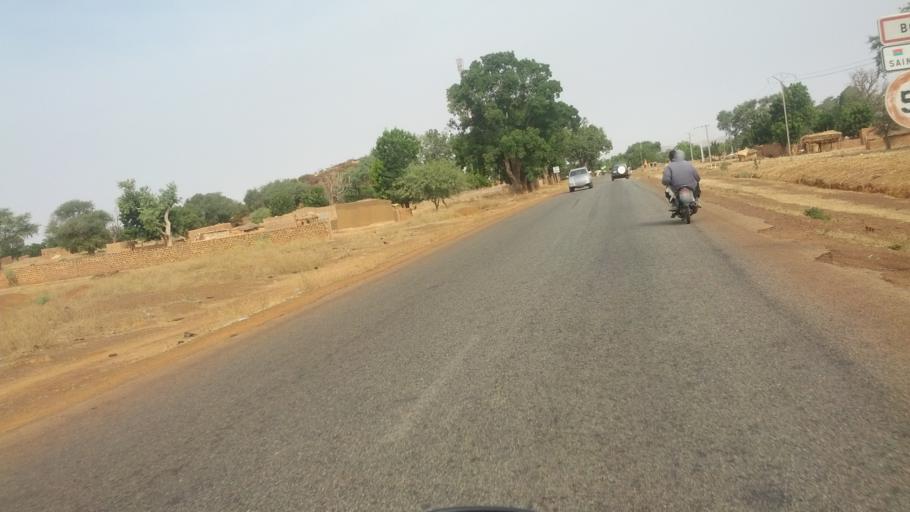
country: BF
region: Centre-Nord
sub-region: Province du Sanmatenga
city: Kaya
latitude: 12.8994
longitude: -1.0777
